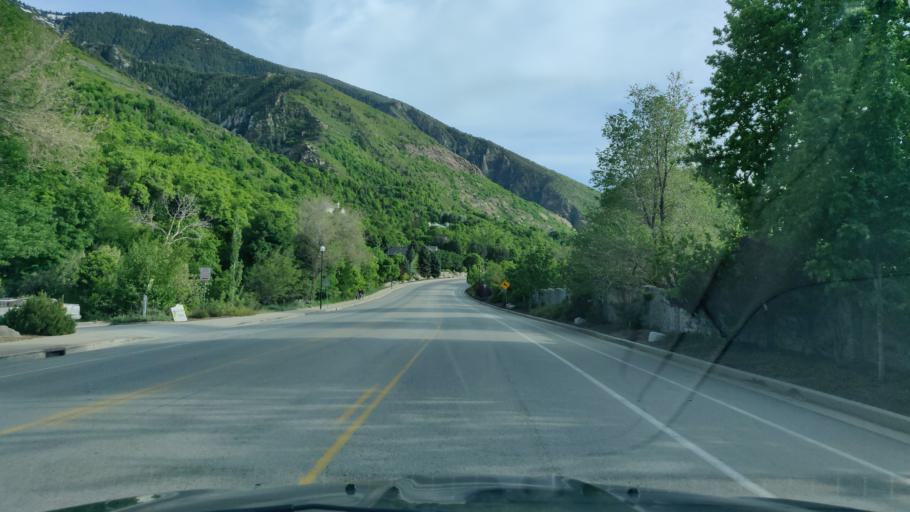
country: US
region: Utah
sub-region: Salt Lake County
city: Granite
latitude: 40.5475
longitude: -111.8066
